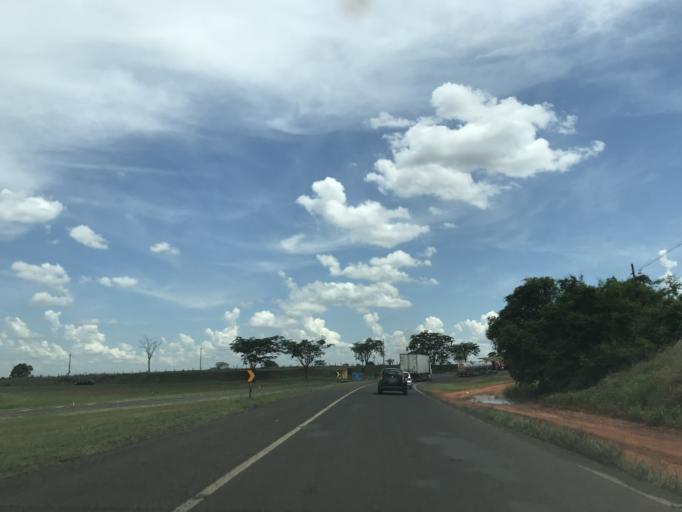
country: BR
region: Sao Paulo
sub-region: Nova Granada
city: Nova Granada
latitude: -20.3255
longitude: -49.2126
